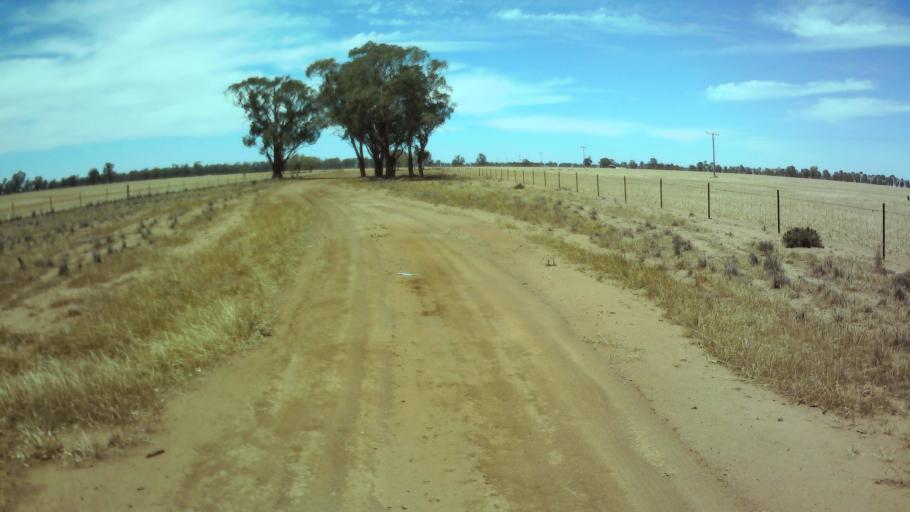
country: AU
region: New South Wales
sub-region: Weddin
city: Grenfell
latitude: -33.8924
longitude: 147.8023
